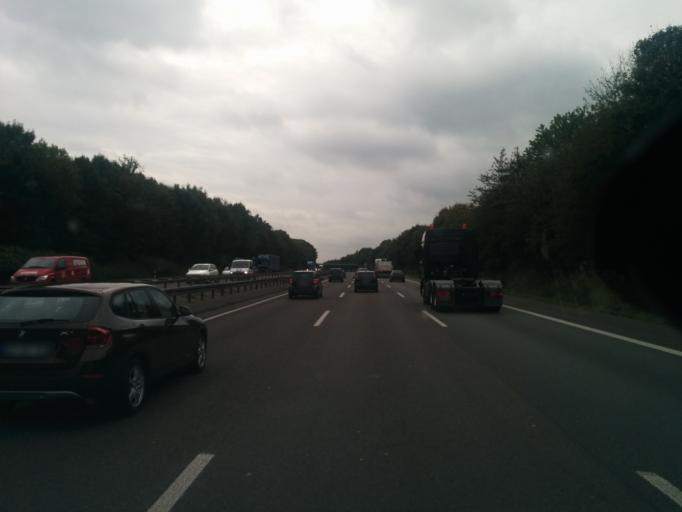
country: DE
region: North Rhine-Westphalia
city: Burscheid
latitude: 51.1128
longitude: 7.1472
